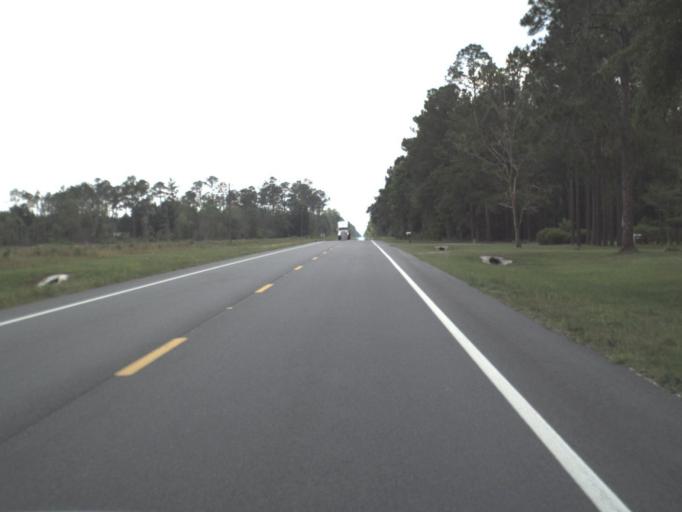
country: US
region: Florida
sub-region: Columbia County
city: Five Points
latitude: 30.3749
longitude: -82.6233
